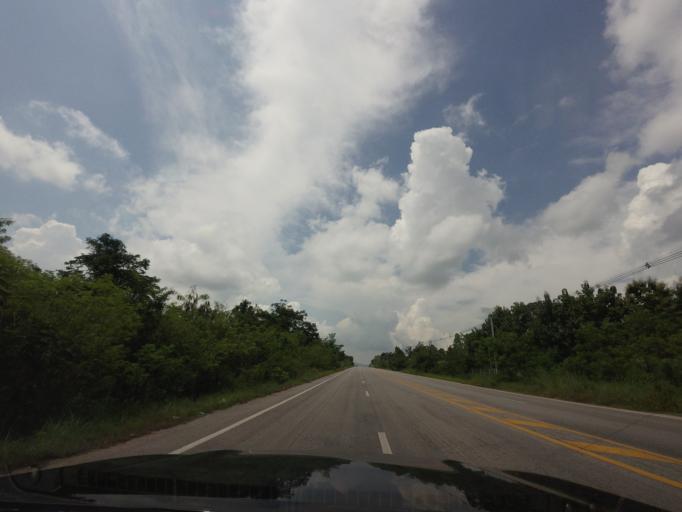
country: TH
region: Khon Kaen
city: Phu Wiang
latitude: 16.6795
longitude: 102.3448
